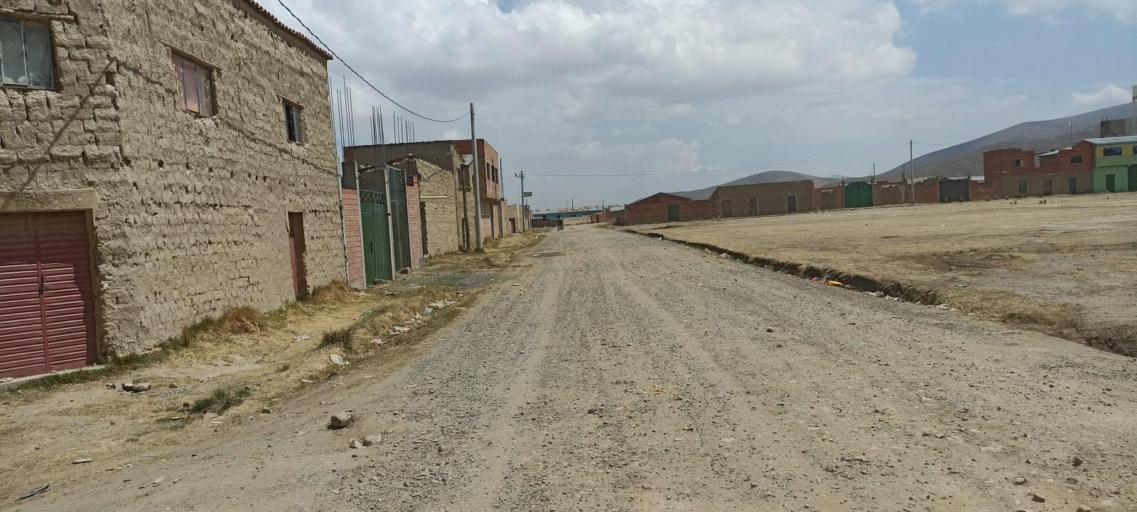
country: BO
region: La Paz
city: Batallas
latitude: -16.4084
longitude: -68.5425
